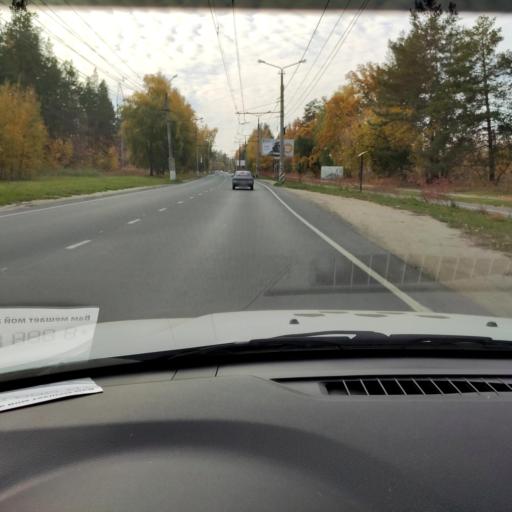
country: RU
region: Samara
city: Tol'yatti
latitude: 53.4950
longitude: 49.3868
